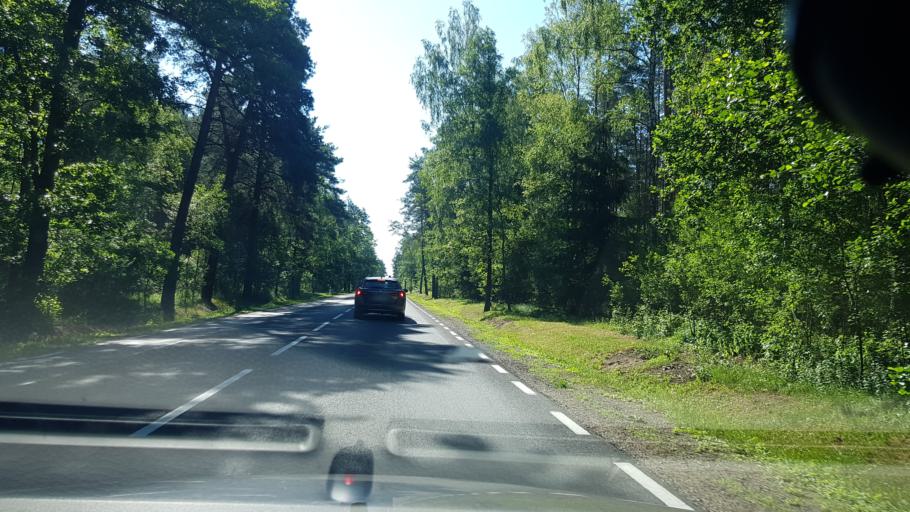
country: PL
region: Masovian Voivodeship
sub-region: Powiat wyszkowski
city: Branszczyk
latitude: 52.5679
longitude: 21.5487
